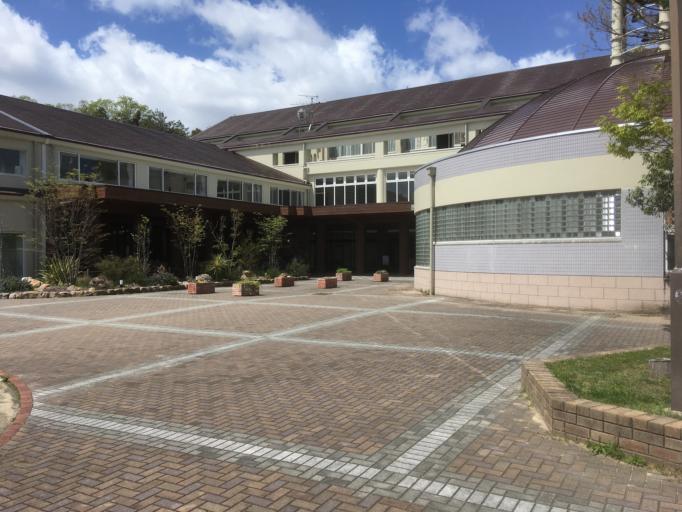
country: JP
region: Nara
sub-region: Ikoma-shi
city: Ikoma
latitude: 34.7026
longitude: 135.6788
